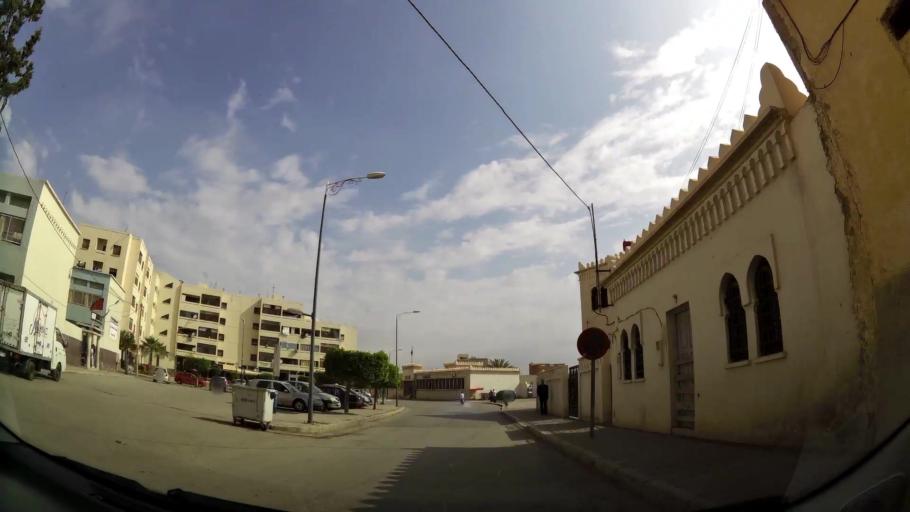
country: MA
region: Oriental
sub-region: Oujda-Angad
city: Oujda
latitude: 34.6853
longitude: -1.9066
